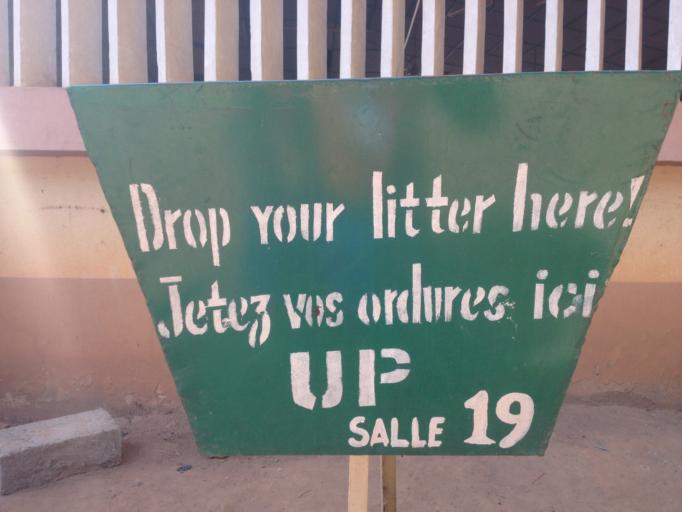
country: BJ
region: Borgou
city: Parakou
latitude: 9.3375
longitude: 2.6462
